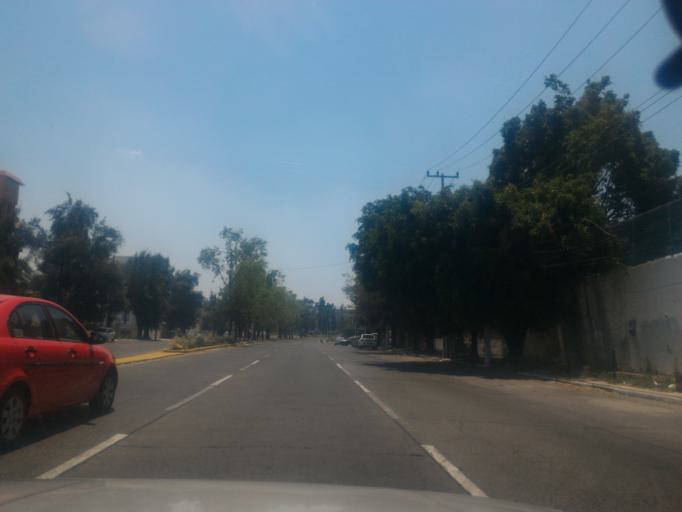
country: MX
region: Jalisco
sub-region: Zapopan
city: Zapopan
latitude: 20.7144
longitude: -103.3856
